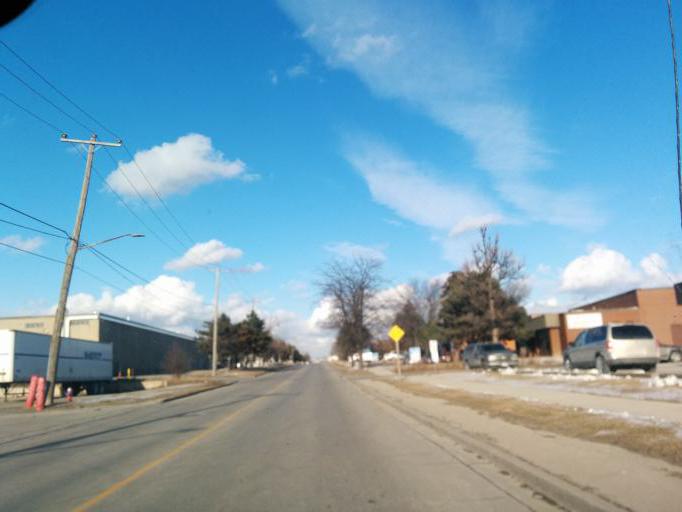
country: CA
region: Ontario
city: Mississauga
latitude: 43.6333
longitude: -79.6303
